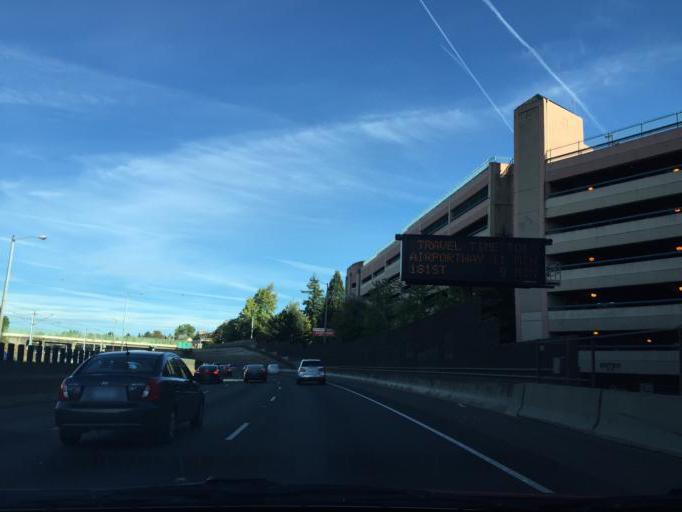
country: US
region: Oregon
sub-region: Multnomah County
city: Portland
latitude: 45.5283
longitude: -122.6119
